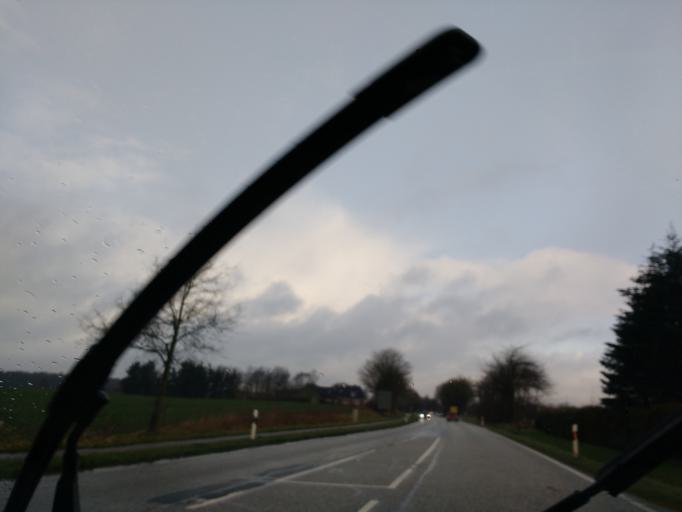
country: DE
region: Schleswig-Holstein
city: Goosefeld
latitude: 54.4375
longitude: 9.8171
